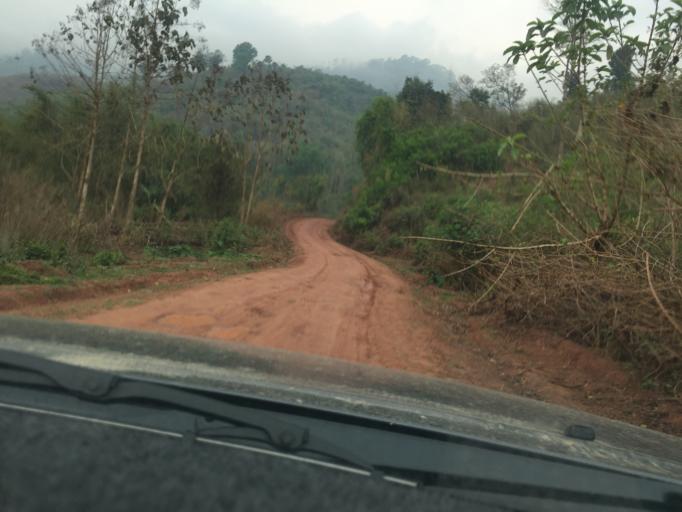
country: TH
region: Nan
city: Bo Kluea
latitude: 18.8469
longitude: 101.4142
